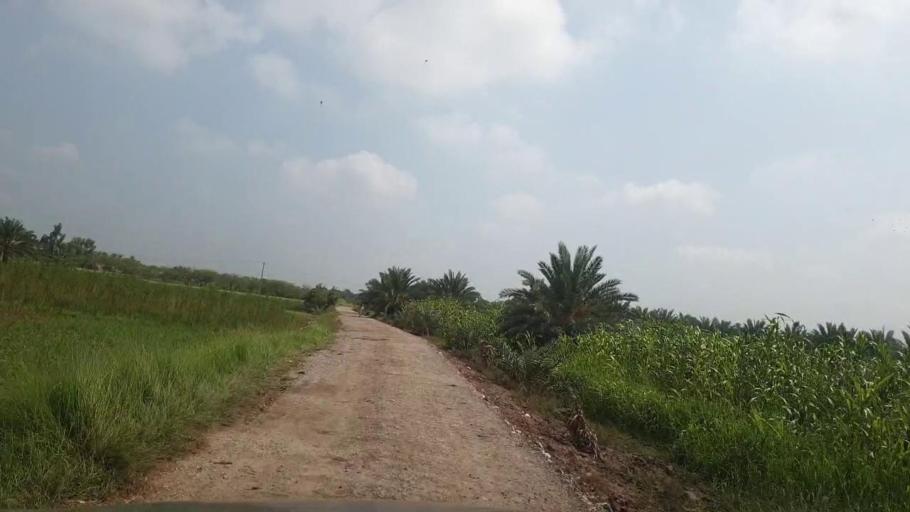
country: PK
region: Sindh
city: Pir jo Goth
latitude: 27.6035
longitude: 68.6959
